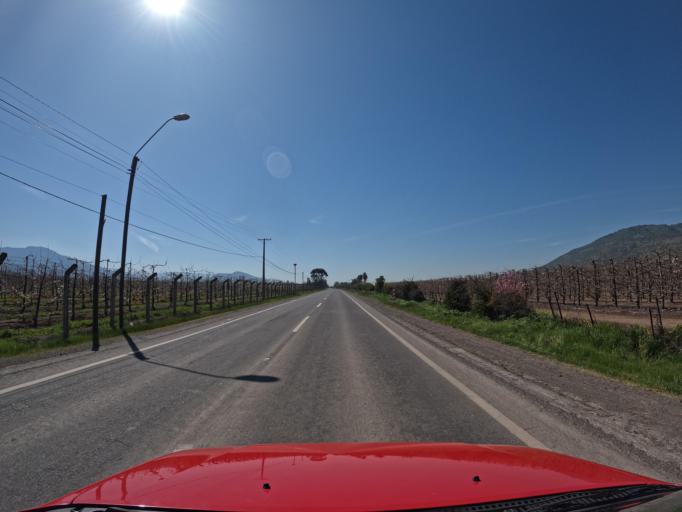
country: CL
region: Maule
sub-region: Provincia de Curico
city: Rauco
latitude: -35.0150
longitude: -71.4213
